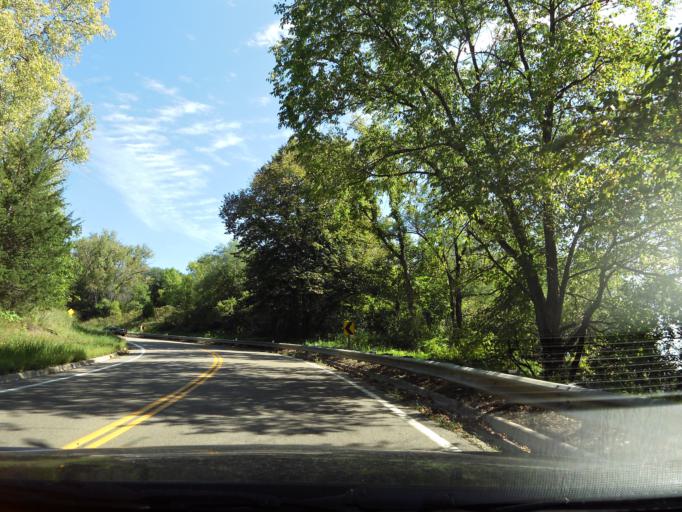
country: US
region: Minnesota
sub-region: Scott County
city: Shakopee
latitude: 44.8135
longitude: -93.5406
